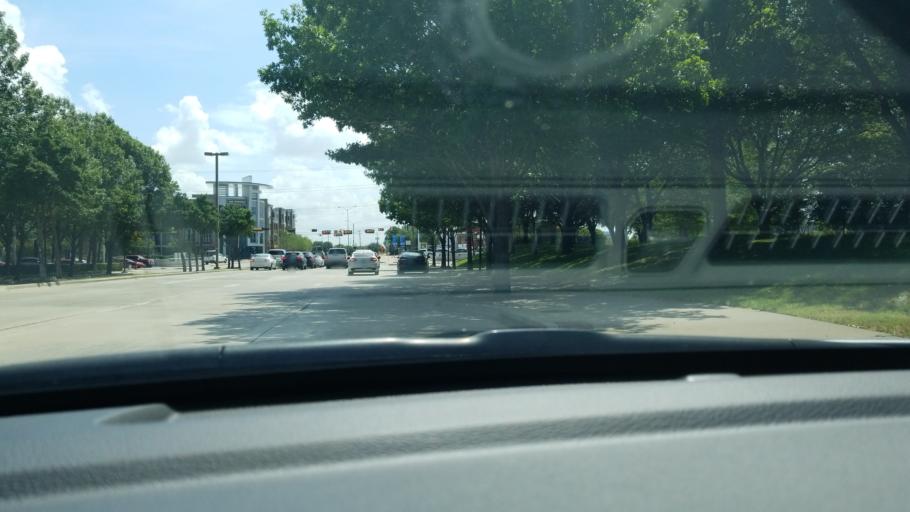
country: US
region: Texas
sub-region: Dallas County
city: Addison
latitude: 32.9594
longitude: -96.8225
